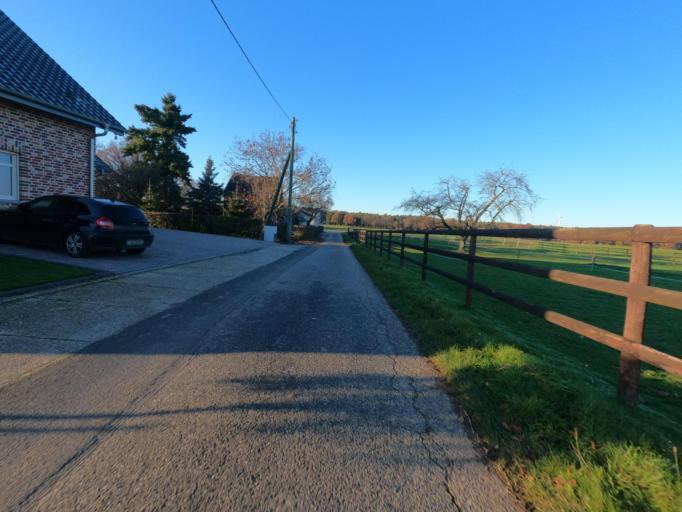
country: DE
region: North Rhine-Westphalia
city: Geilenkirchen
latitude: 50.9909
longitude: 6.0882
